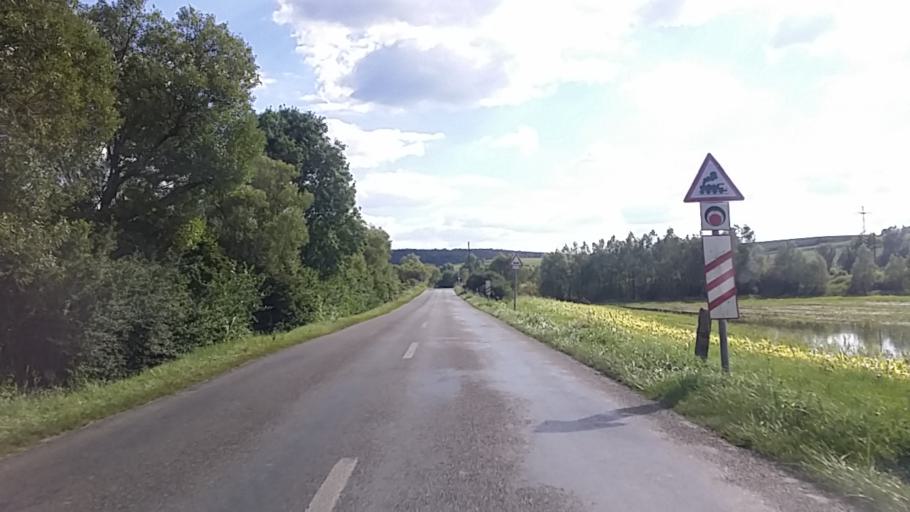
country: HU
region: Baranya
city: Sasd
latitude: 46.2180
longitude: 18.1080
